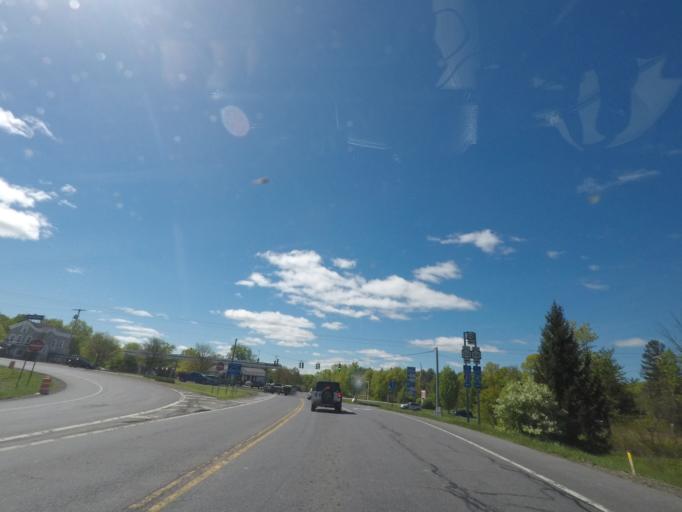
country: US
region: New York
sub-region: Ulster County
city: Saugerties
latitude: 42.0841
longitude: -73.9762
